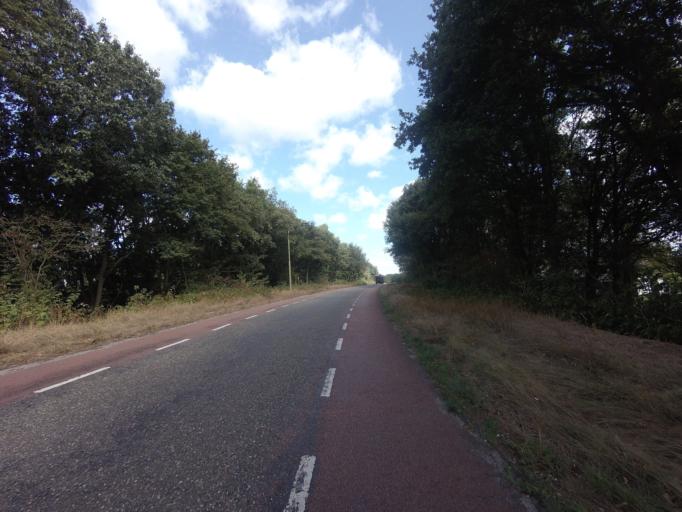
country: NL
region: North Brabant
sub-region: Gemeente Landerd
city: Schaijk
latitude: 51.7456
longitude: 5.6085
